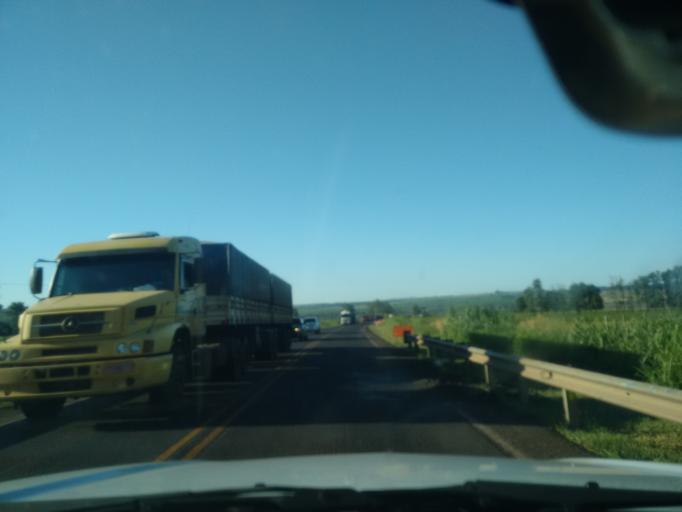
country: BR
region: Mato Grosso do Sul
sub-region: Eldorado
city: Eldorado
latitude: -23.8546
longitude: -54.3362
